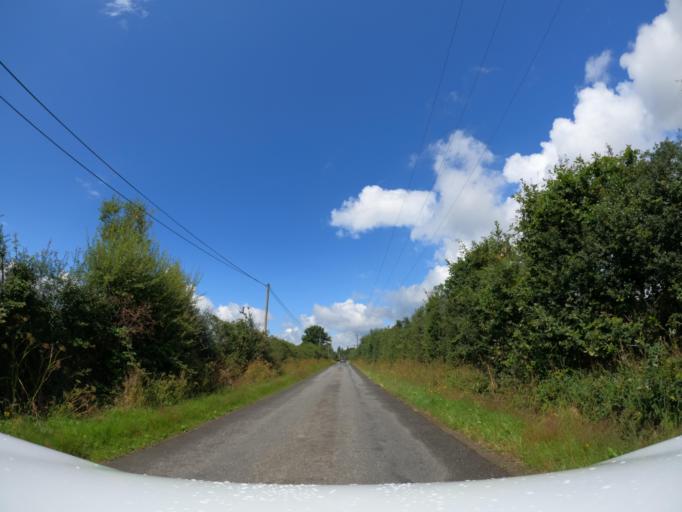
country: FR
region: Pays de la Loire
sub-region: Departement de la Loire-Atlantique
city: Saint-Mars-du-Desert
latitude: 47.3896
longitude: -1.4034
